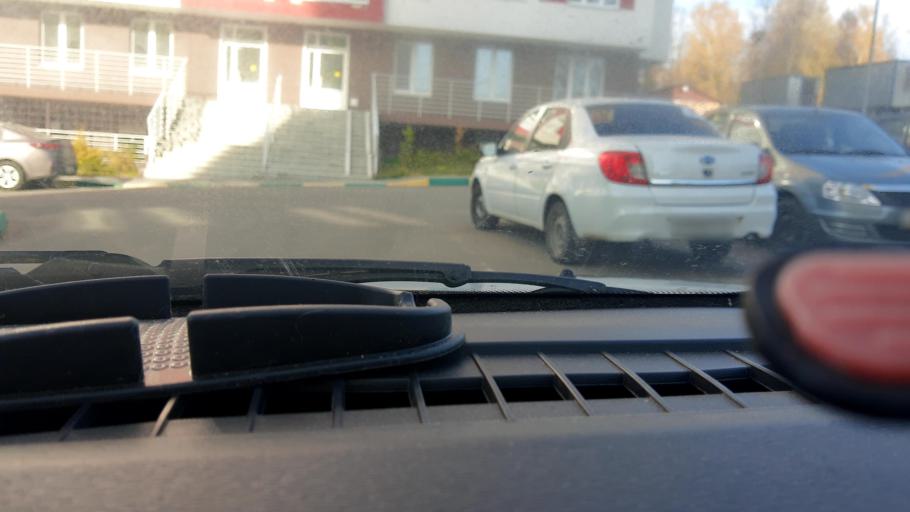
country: RU
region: Nizjnij Novgorod
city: Nizhniy Novgorod
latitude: 56.2592
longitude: 43.9828
